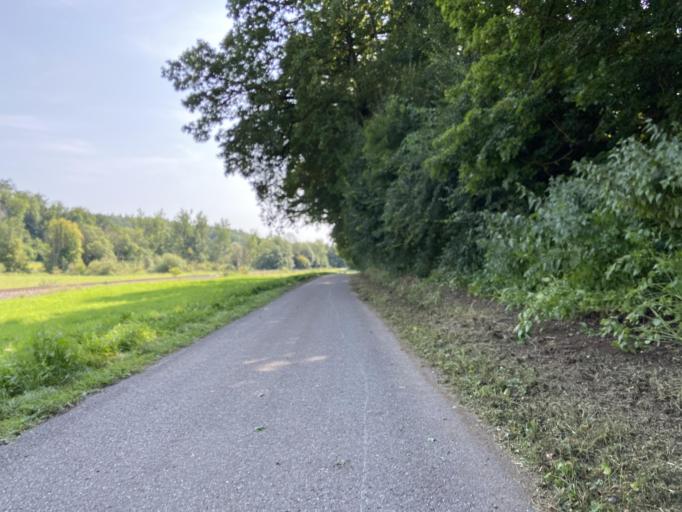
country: DE
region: Baden-Wuerttemberg
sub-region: Tuebingen Region
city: Bingen
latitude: 48.0953
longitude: 9.2806
